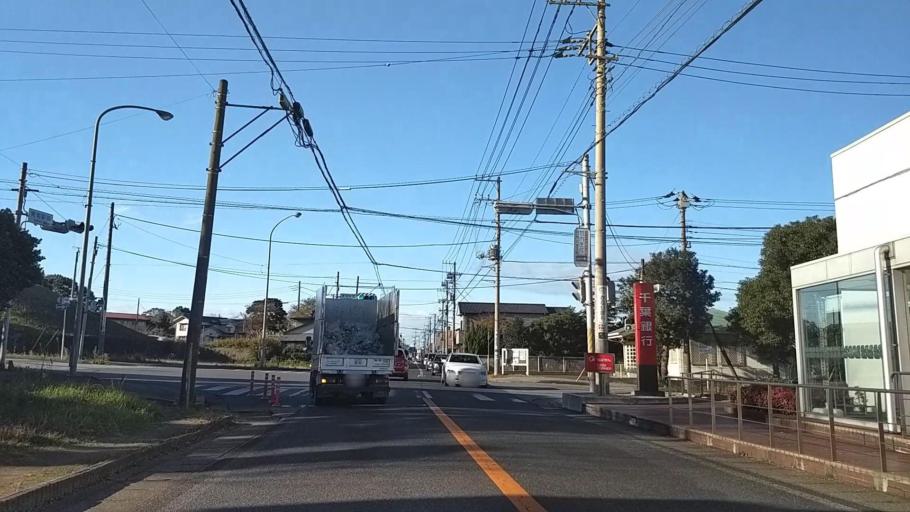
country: JP
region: Chiba
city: Kimitsu
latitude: 35.3316
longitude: 139.8587
